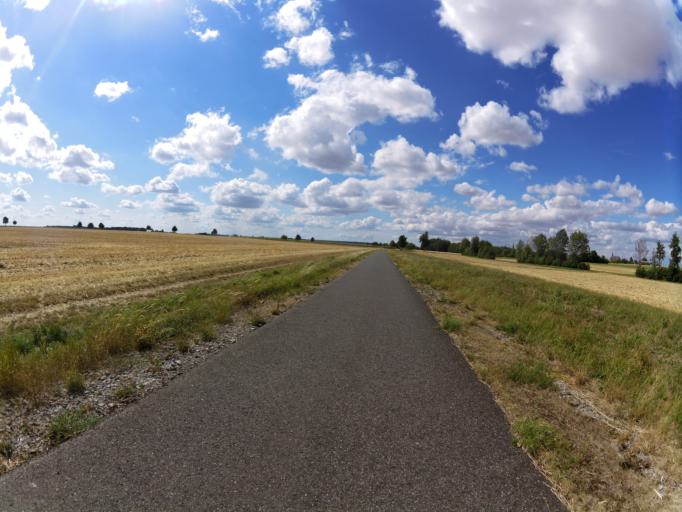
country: DE
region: Bavaria
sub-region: Regierungsbezirk Unterfranken
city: Aub
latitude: 49.5675
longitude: 10.0322
